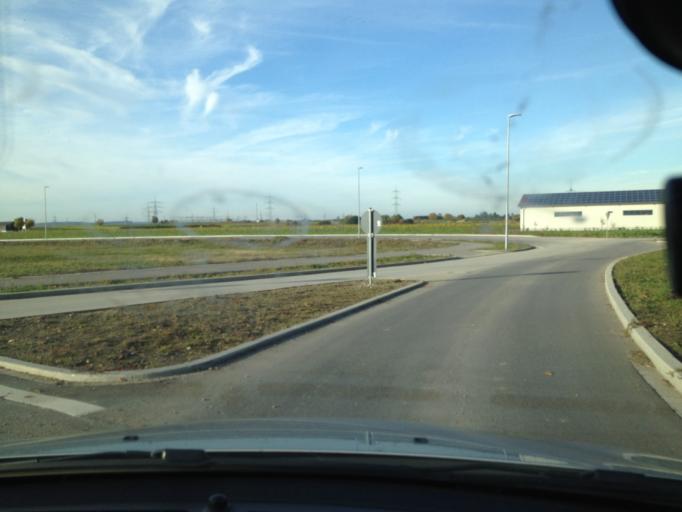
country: DE
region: Bavaria
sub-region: Swabia
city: Oberottmarshausen
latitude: 48.2219
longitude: 10.8488
